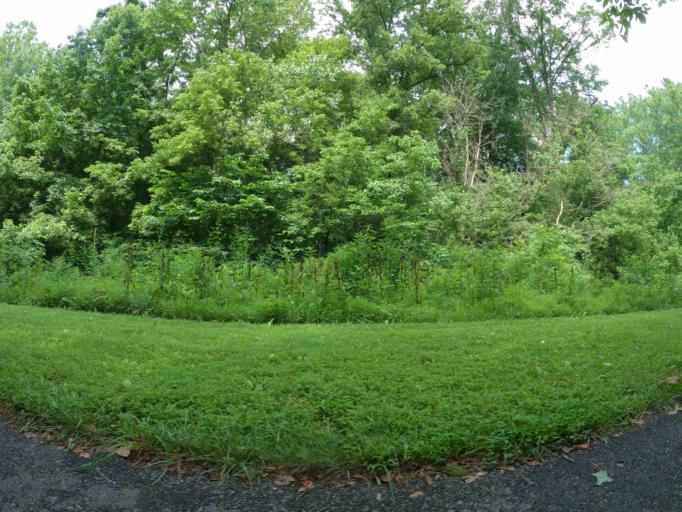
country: US
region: Maryland
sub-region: Frederick County
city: Brunswick
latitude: 39.3198
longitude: -77.6372
